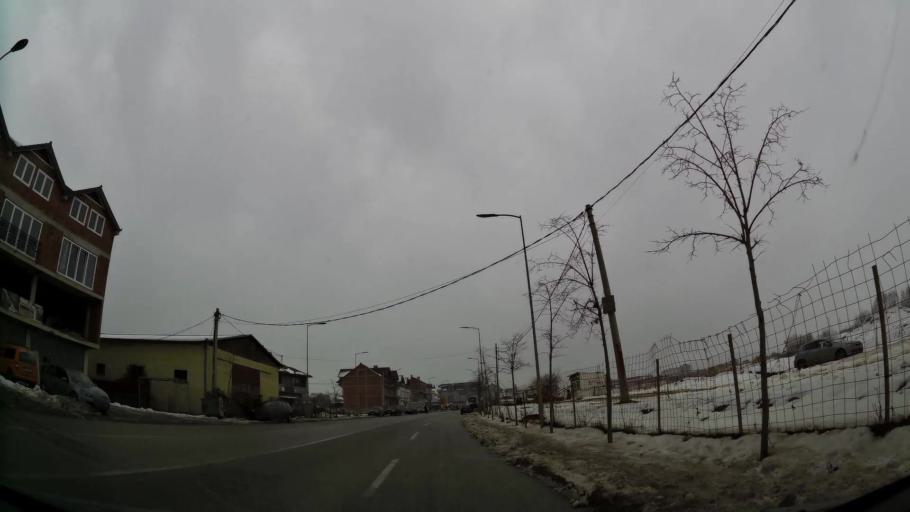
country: XK
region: Pristina
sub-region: Komuna e Prishtines
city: Pristina
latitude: 42.7008
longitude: 21.1585
